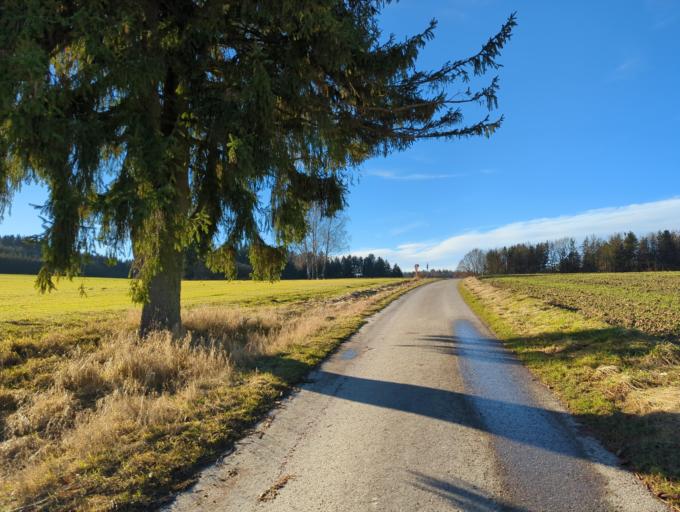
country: DE
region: Bavaria
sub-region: Swabia
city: Roggenburg
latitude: 48.2714
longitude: 10.2176
